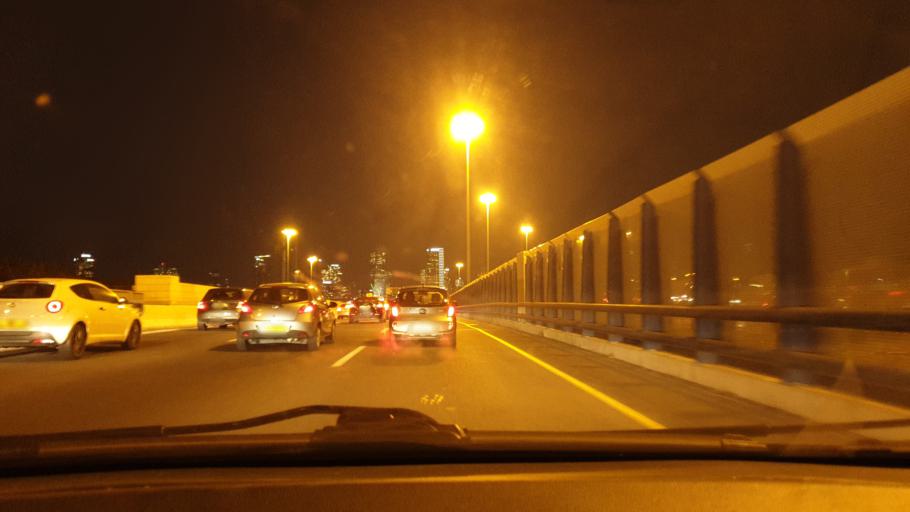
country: IL
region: Tel Aviv
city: Yafo
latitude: 32.0472
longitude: 34.7840
